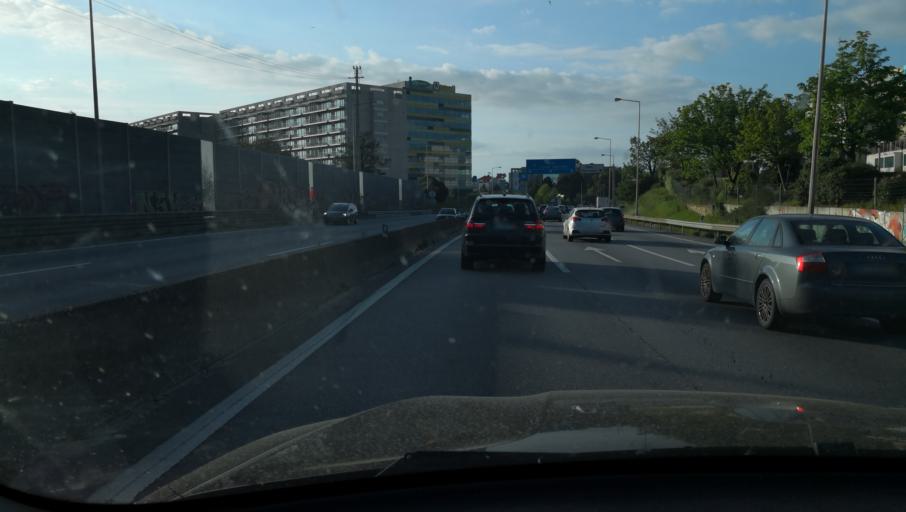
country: PT
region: Porto
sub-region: Vila Nova de Gaia
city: Canidelo
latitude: 41.1403
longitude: -8.6379
